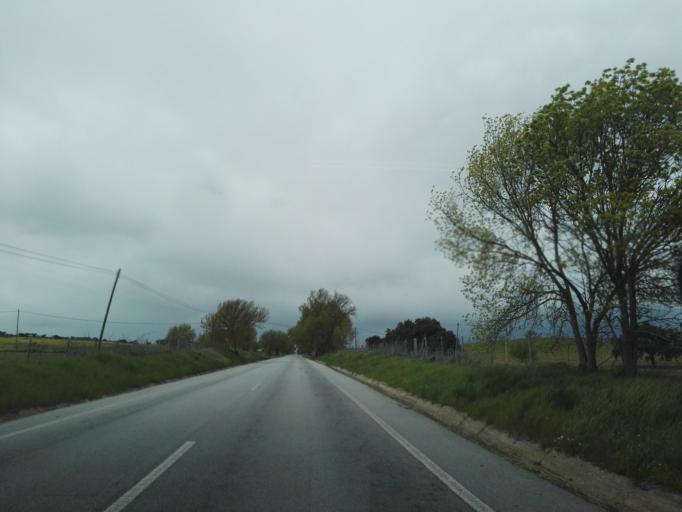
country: PT
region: Portalegre
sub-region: Elvas
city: Elvas
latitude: 38.9612
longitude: -7.2203
